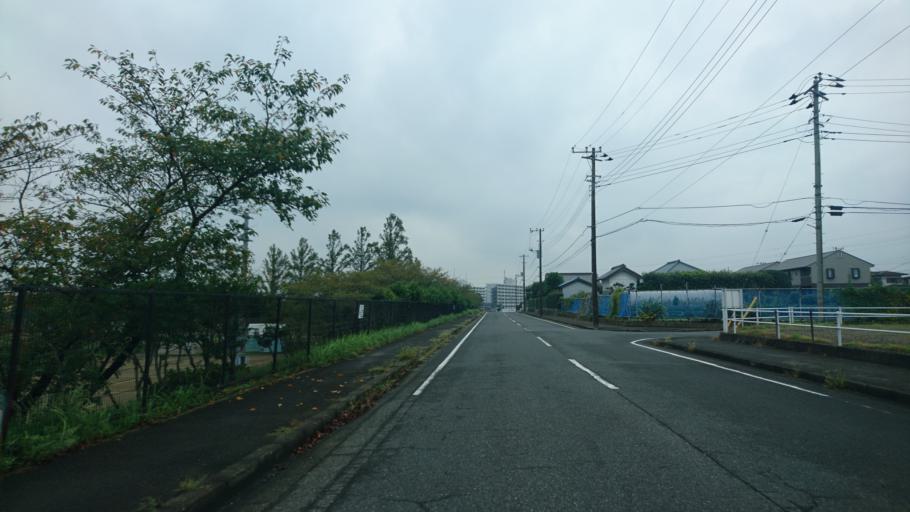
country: JP
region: Chiba
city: Kimitsu
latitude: 35.3262
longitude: 139.9281
